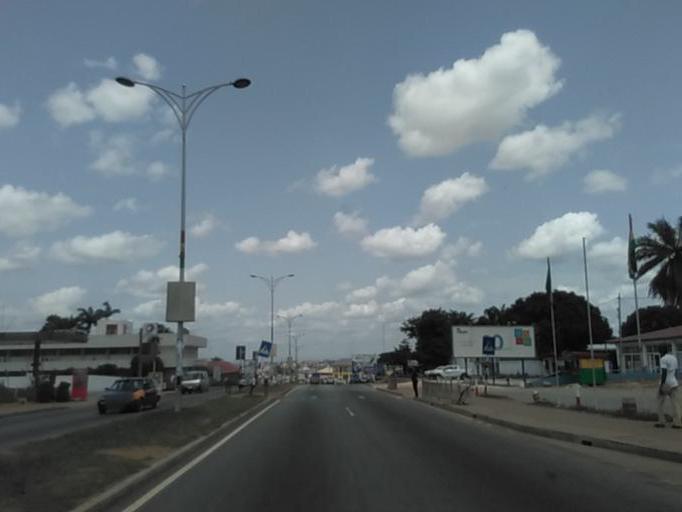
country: GH
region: Ashanti
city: Kumasi
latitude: 6.6662
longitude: -1.6046
